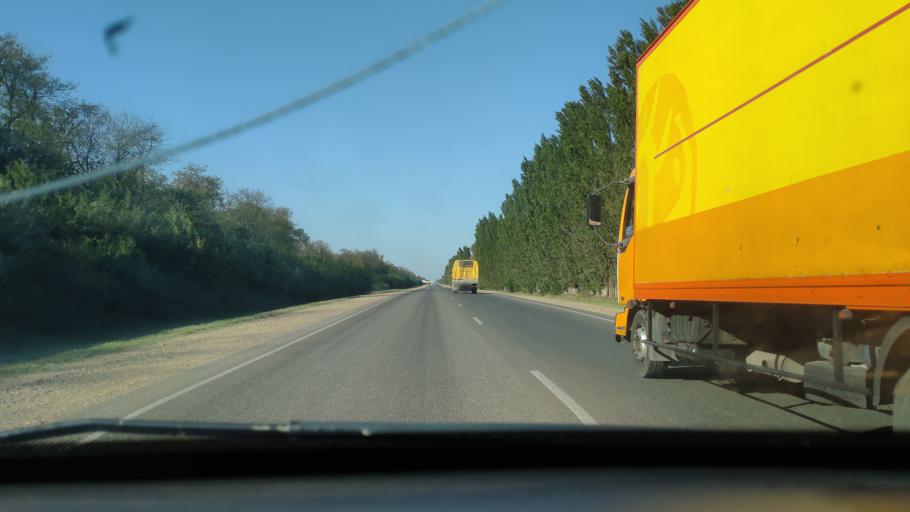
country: RU
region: Krasnodarskiy
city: Novotitarovskaya
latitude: 45.2645
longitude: 39.0012
